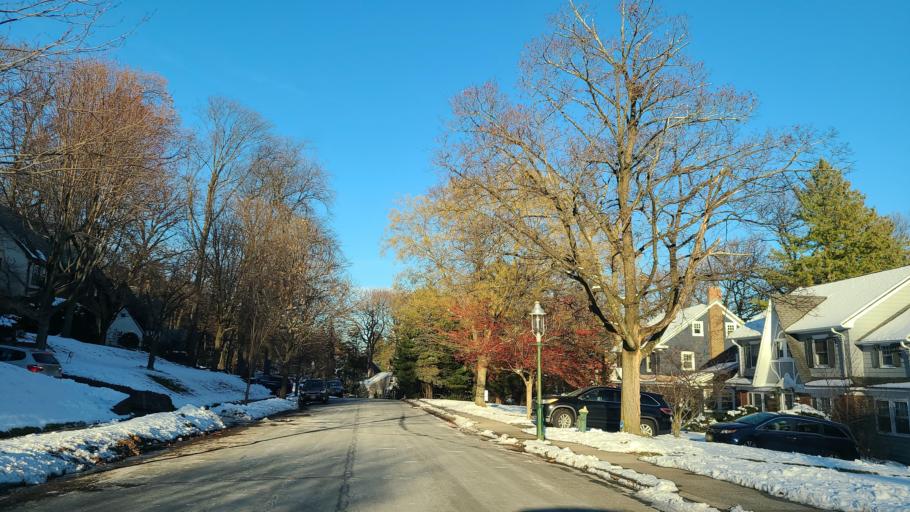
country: US
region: New Jersey
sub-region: Essex County
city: South Orange
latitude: 40.7541
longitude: -74.2687
